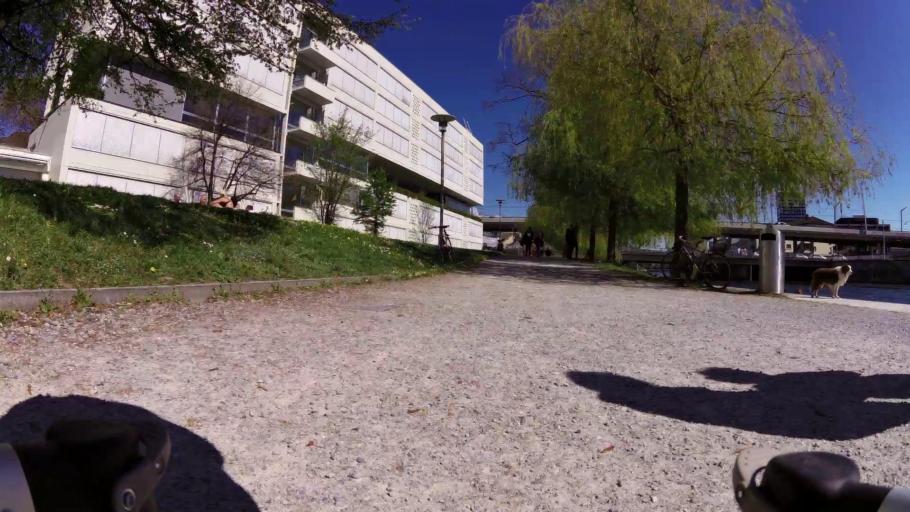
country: CH
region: Zurich
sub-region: Bezirk Zuerich
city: Zuerich (Kreis 5) / Gewerbeschule
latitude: 47.3894
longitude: 8.5317
